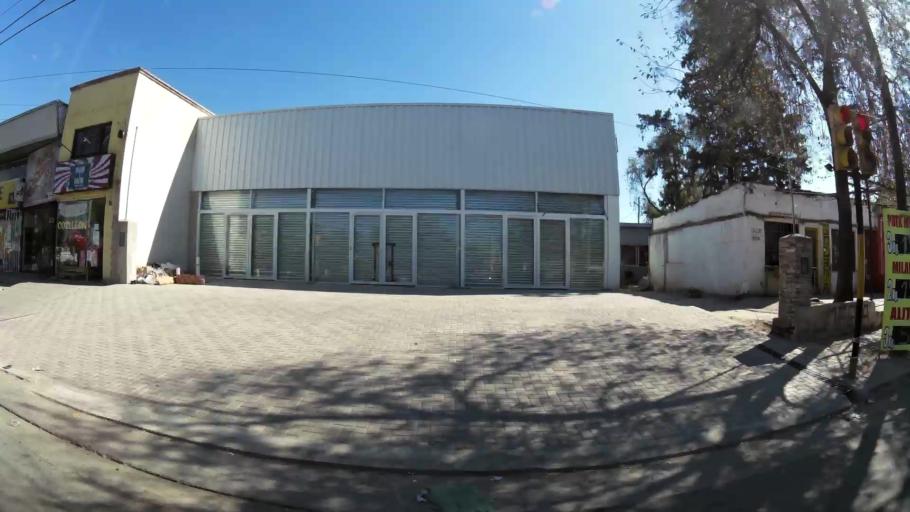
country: AR
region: Cordoba
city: Villa Allende
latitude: -31.3252
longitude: -64.2685
